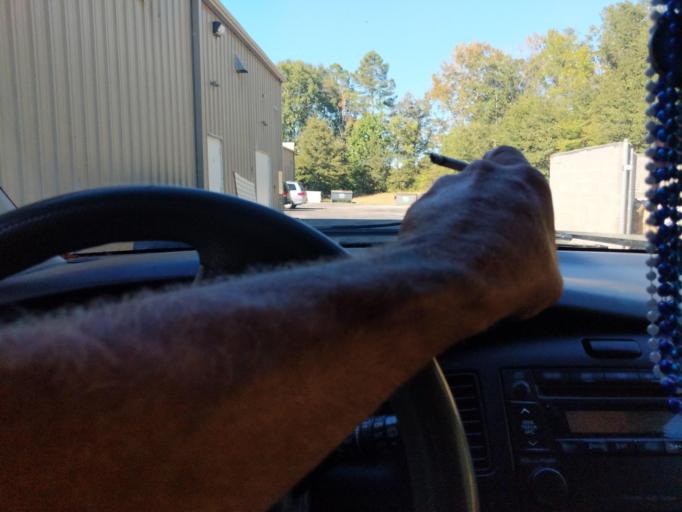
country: US
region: Alabama
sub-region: Houston County
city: Dothan
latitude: 31.1786
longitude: -85.4003
